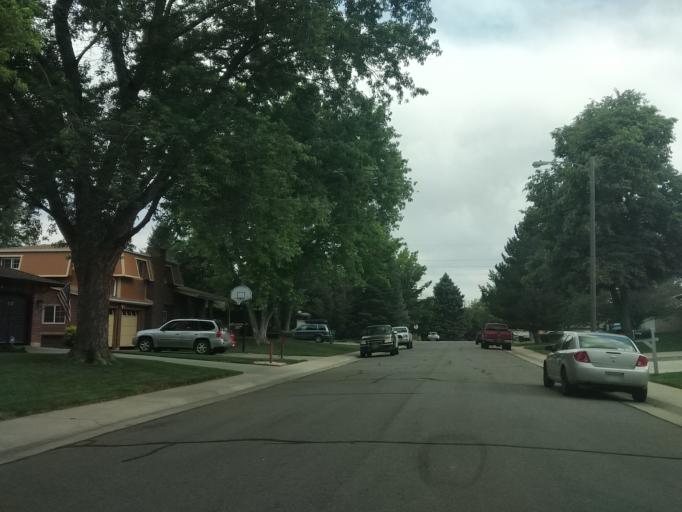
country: US
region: Colorado
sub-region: Jefferson County
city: Lakewood
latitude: 39.6977
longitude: -105.1025
